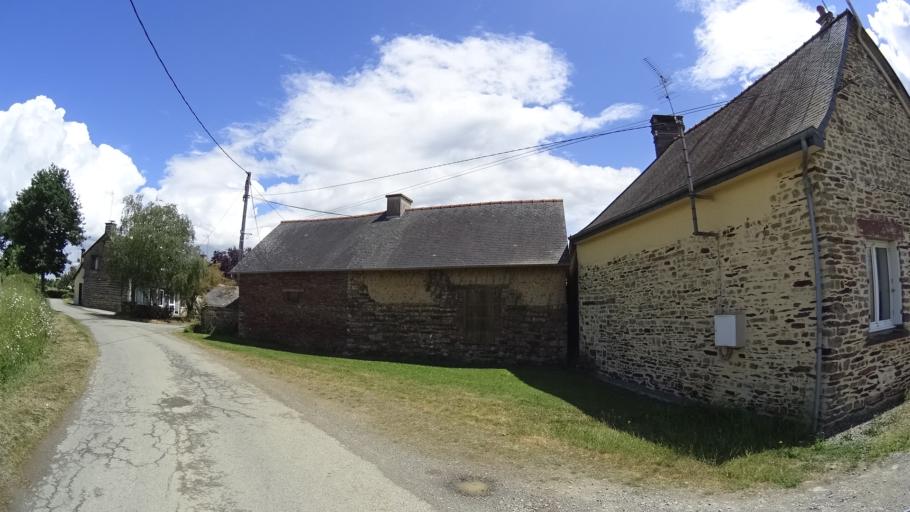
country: FR
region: Brittany
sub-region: Departement d'Ille-et-Vilaine
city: Crevin
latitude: 47.9401
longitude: -1.6968
